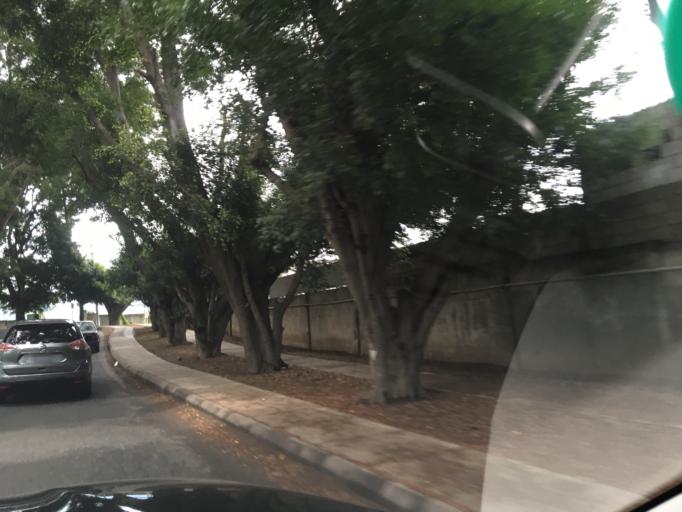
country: GT
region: Guatemala
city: Villa Nueva
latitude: 14.5103
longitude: -90.5824
